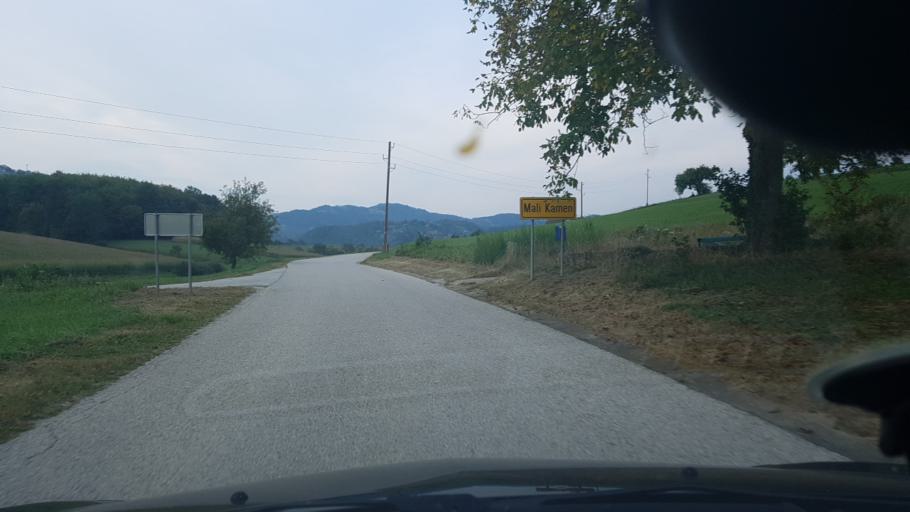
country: SI
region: Krsko
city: Senovo
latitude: 46.0270
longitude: 15.5066
